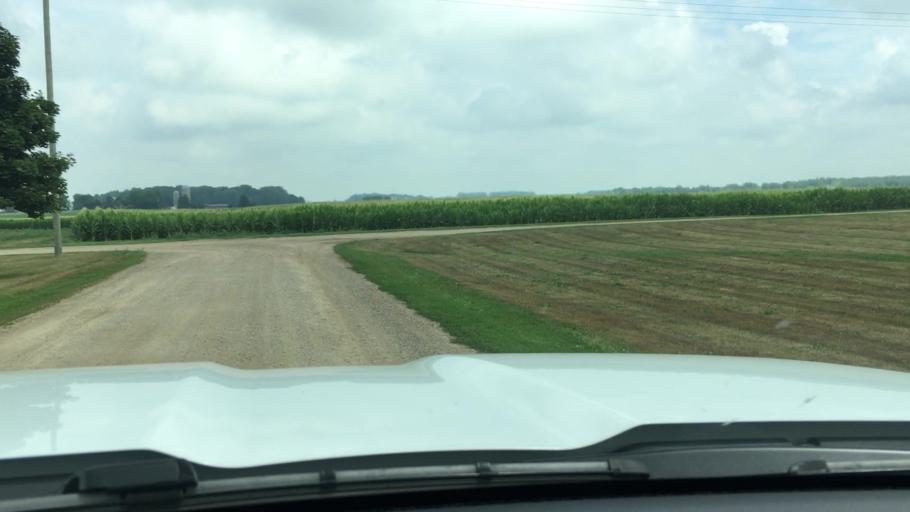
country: US
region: Michigan
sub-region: Sanilac County
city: Marlette
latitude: 43.3515
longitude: -82.9730
